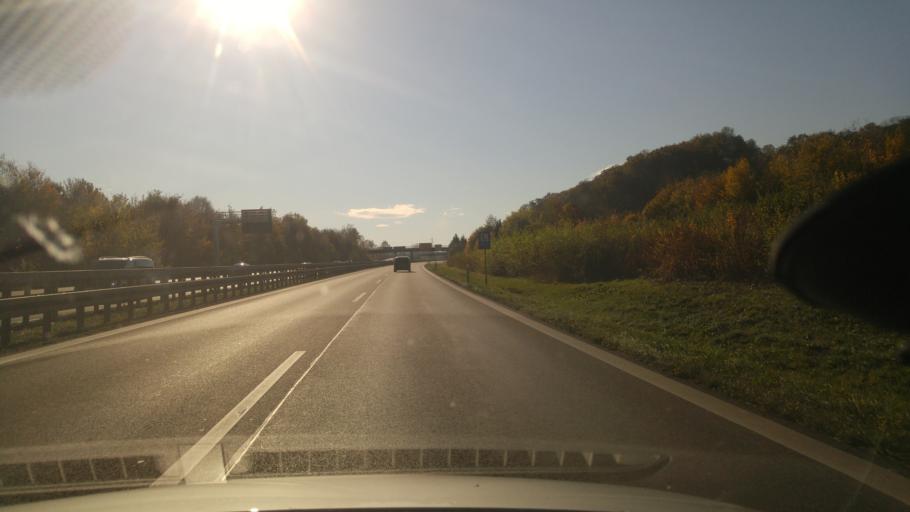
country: DE
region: Baden-Wuerttemberg
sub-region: Regierungsbezirk Stuttgart
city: Wernau
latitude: 48.7021
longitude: 9.4123
